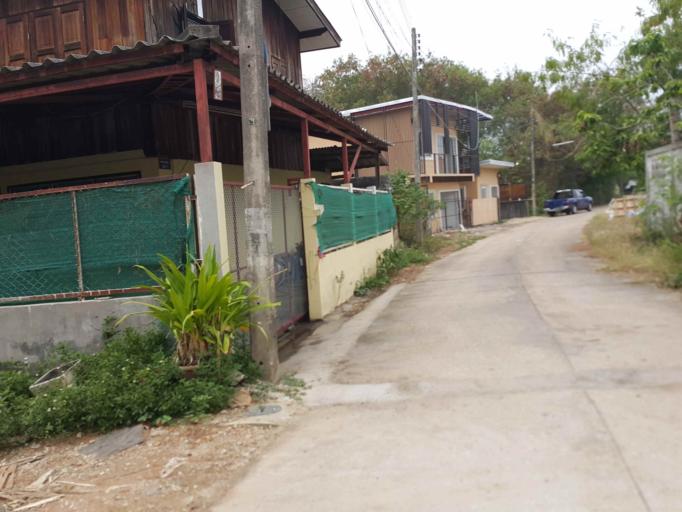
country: TH
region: Chiang Mai
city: Saraphi
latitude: 18.7524
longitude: 99.0186
